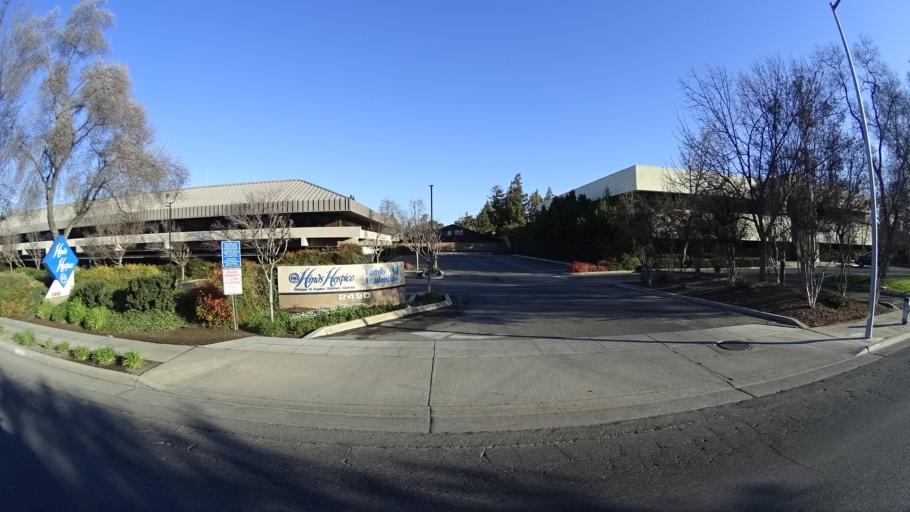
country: US
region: California
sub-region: Fresno County
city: Fresno
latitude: 36.8083
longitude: -119.8367
